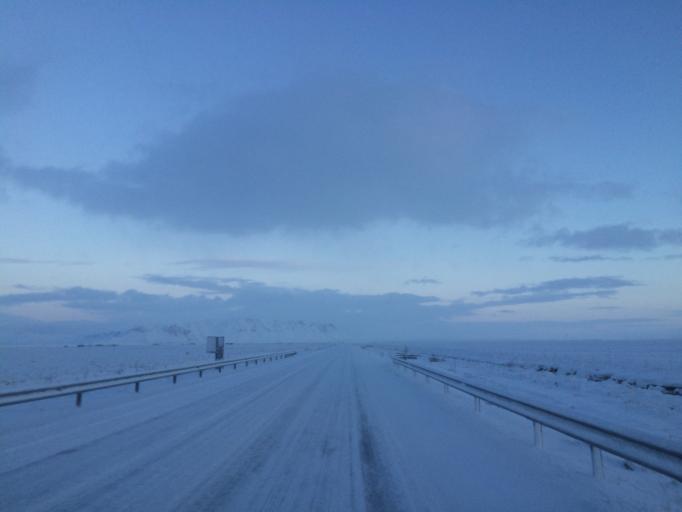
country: IS
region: South
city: Selfoss
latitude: 63.8834
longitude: -21.0852
